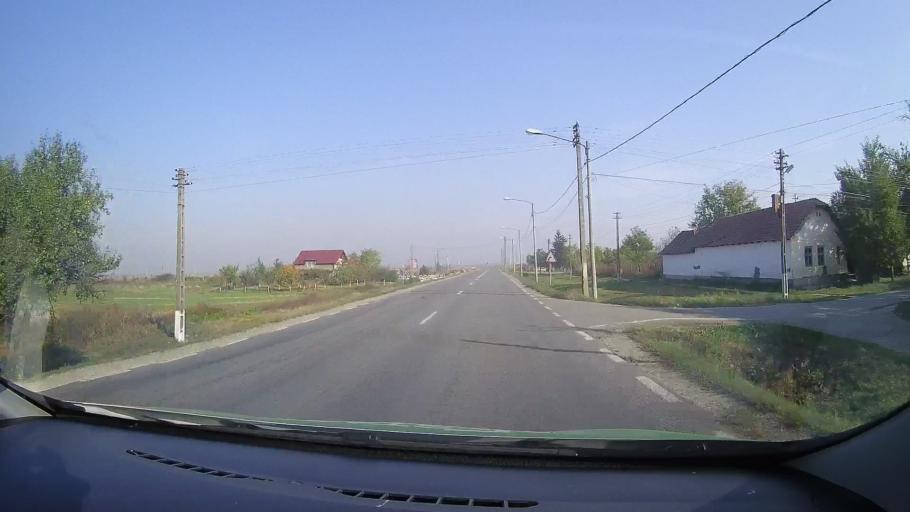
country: RO
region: Arad
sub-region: Comuna Pilu
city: Pilu
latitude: 46.5814
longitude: 21.3435
